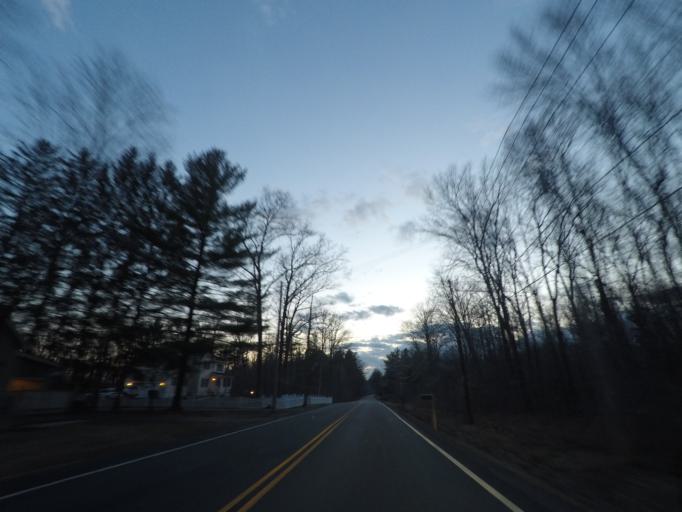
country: US
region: New York
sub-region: Schenectady County
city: Niskayuna
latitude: 42.8327
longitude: -73.8021
